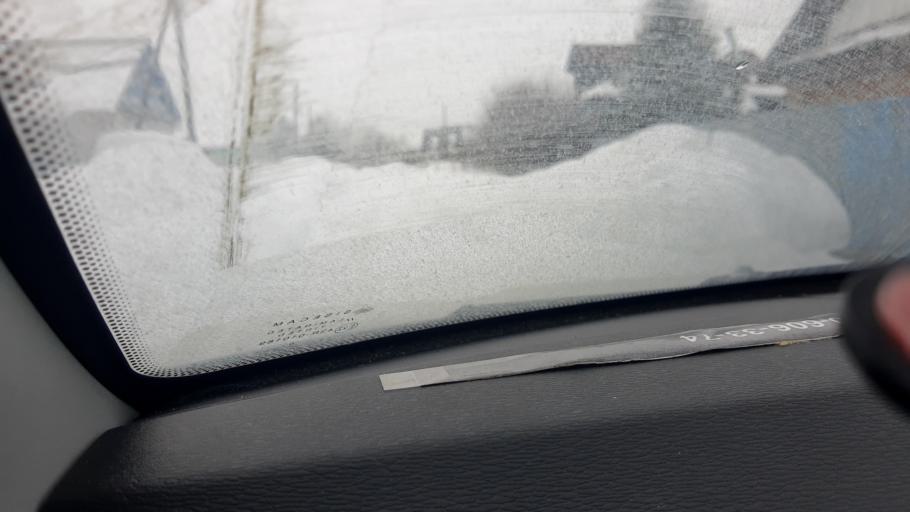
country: RU
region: Nizjnij Novgorod
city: Sitniki
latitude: 56.5298
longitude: 44.0598
